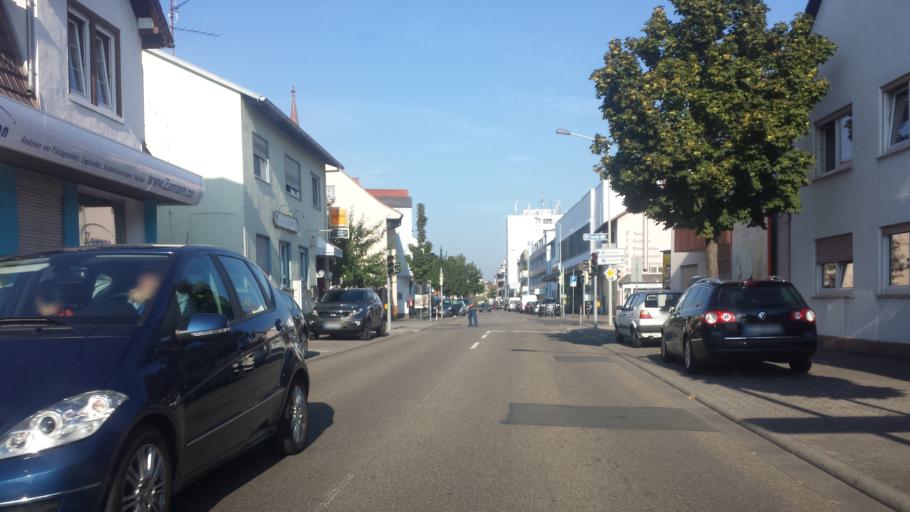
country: DE
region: Hesse
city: Lampertheim
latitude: 49.5937
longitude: 8.4711
